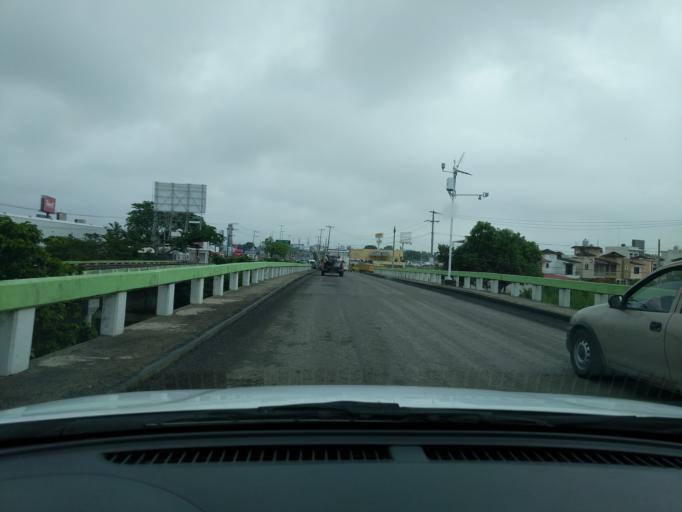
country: MX
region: Tabasco
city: Villahermosa
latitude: 17.9634
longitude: -92.9634
